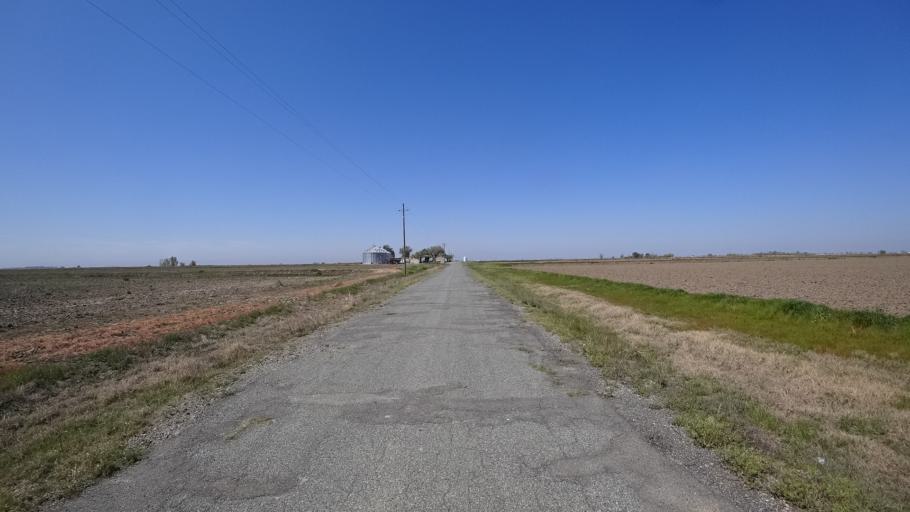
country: US
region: California
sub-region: Glenn County
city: Willows
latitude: 39.4929
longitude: -122.0801
